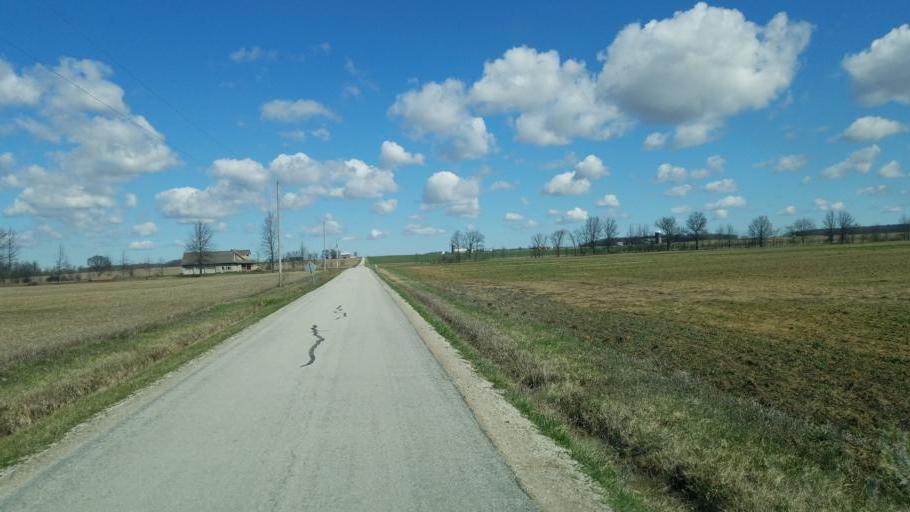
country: US
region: Ohio
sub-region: Sandusky County
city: Mount Carmel
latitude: 41.0681
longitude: -82.9389
